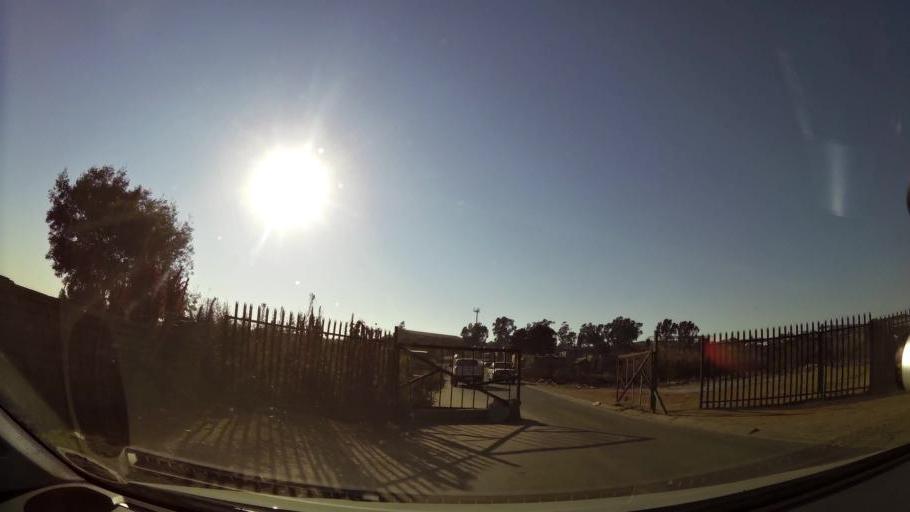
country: ZA
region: Gauteng
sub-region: City of Johannesburg Metropolitan Municipality
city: Modderfontein
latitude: -26.0472
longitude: 28.1566
